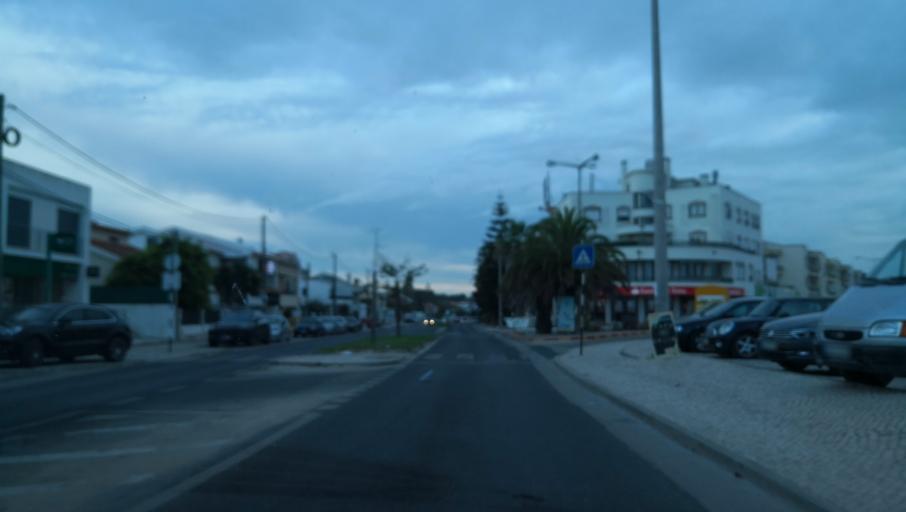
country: PT
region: Setubal
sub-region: Almada
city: Charneca
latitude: 38.6099
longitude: -9.1884
